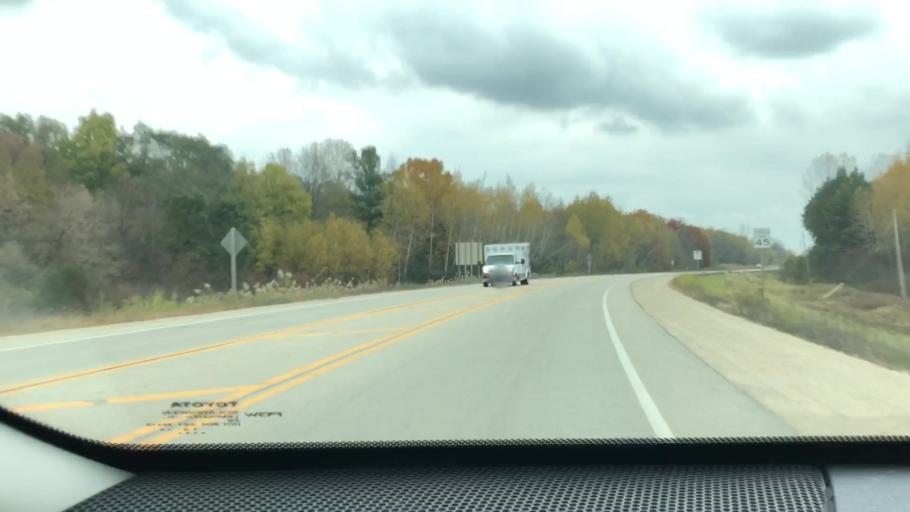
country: US
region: Wisconsin
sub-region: Brown County
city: Oneida
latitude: 44.4995
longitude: -88.1484
